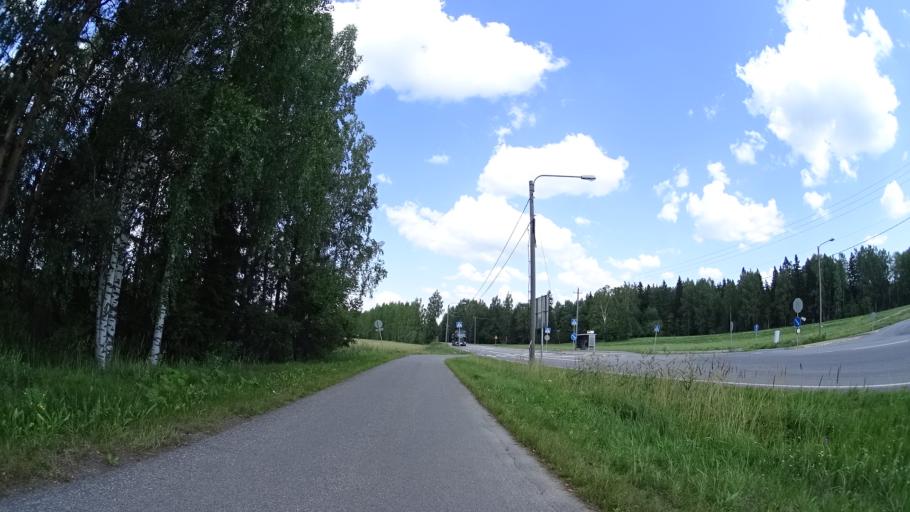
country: FI
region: Uusimaa
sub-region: Helsinki
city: Tuusula
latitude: 60.3360
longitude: 24.9229
